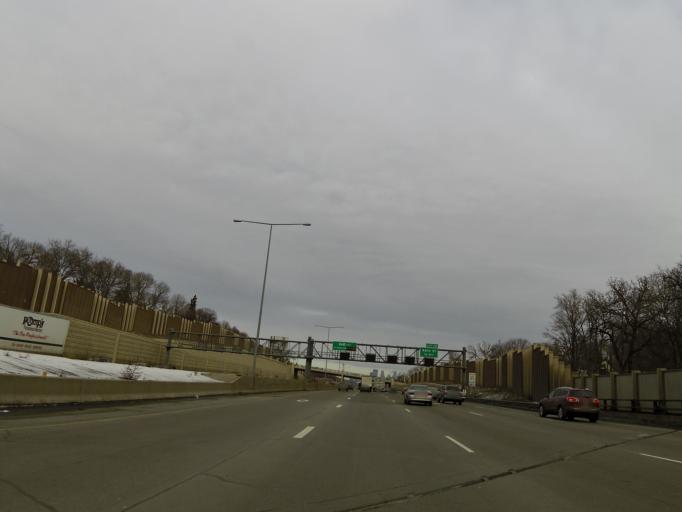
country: US
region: Minnesota
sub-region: Hennepin County
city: Richfield
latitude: 44.9095
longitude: -93.2746
